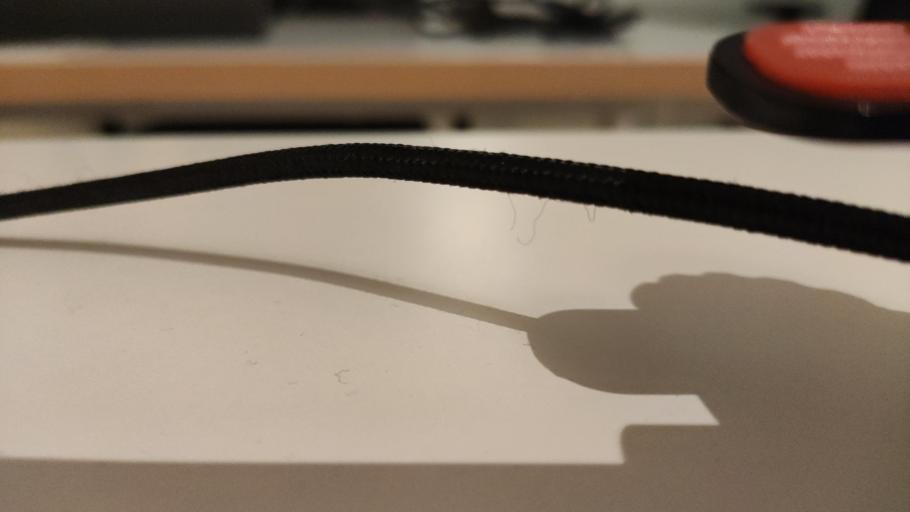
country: RU
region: Moskovskaya
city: Likino-Dulevo
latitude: 55.7118
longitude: 38.9578
